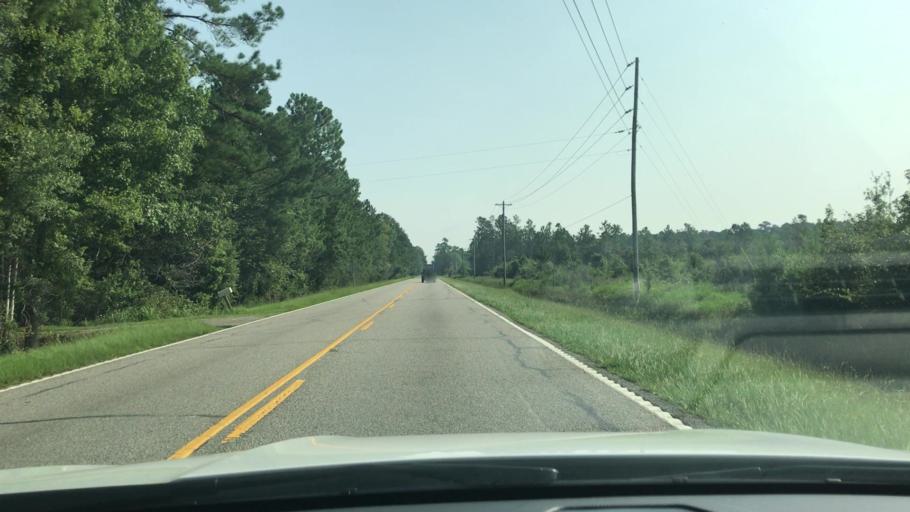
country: US
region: South Carolina
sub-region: Georgetown County
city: Georgetown
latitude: 33.5262
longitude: -79.2420
